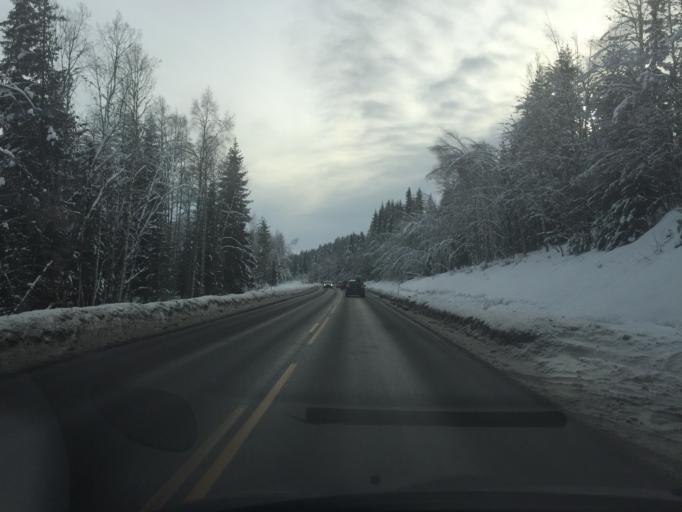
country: NO
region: Hedmark
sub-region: Trysil
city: Innbygda
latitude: 61.2736
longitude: 12.2927
